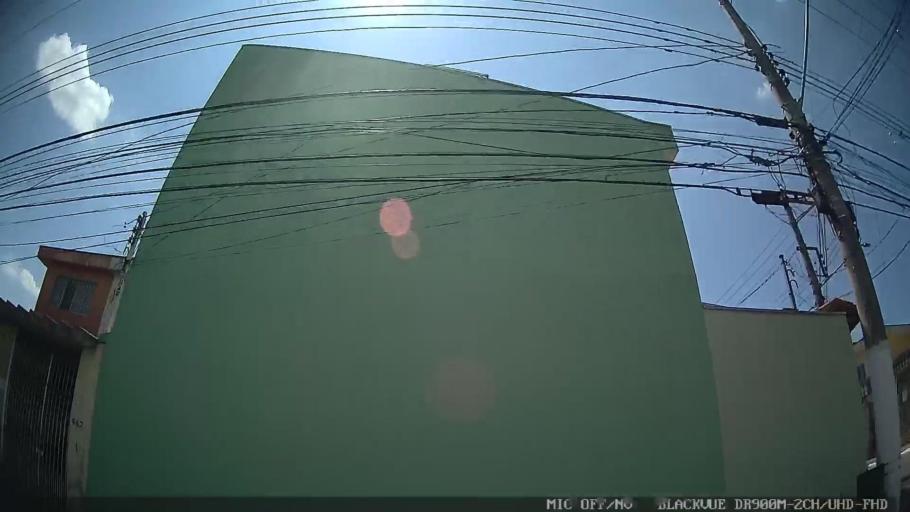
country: BR
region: Sao Paulo
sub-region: Guarulhos
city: Guarulhos
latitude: -23.5203
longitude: -46.4883
